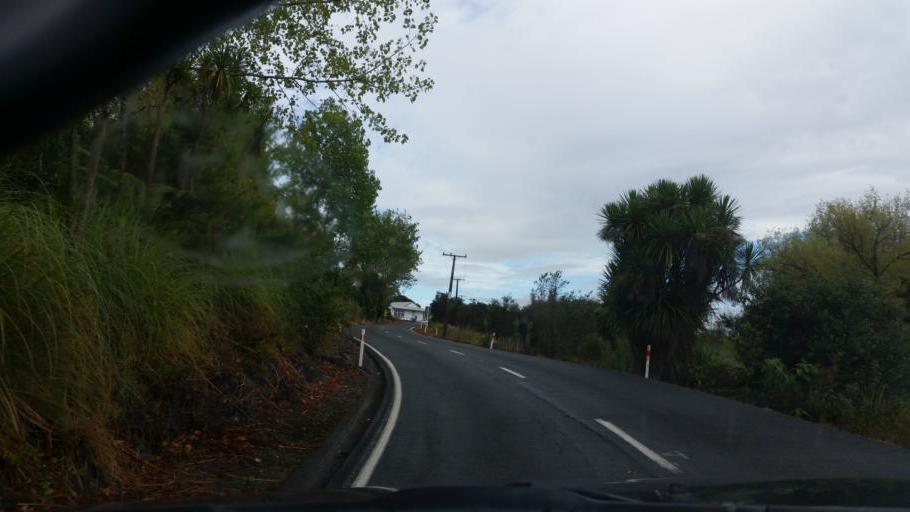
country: NZ
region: Auckland
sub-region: Auckland
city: Wellsford
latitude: -36.1185
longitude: 174.3673
